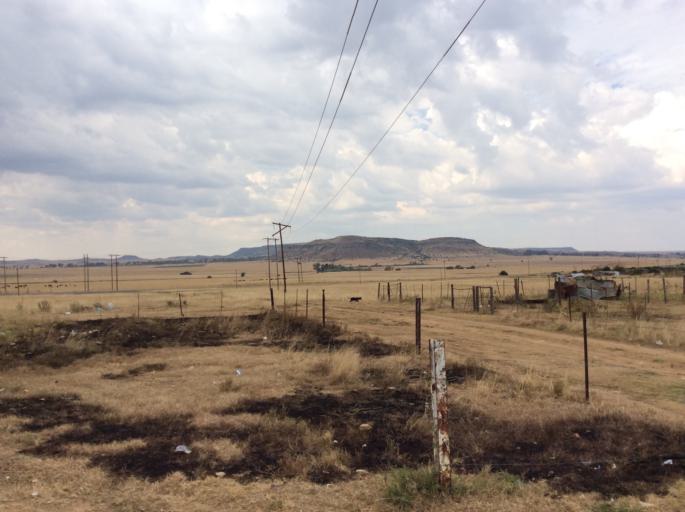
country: ZA
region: Orange Free State
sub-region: Xhariep District Municipality
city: Dewetsdorp
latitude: -29.5767
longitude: 26.6861
